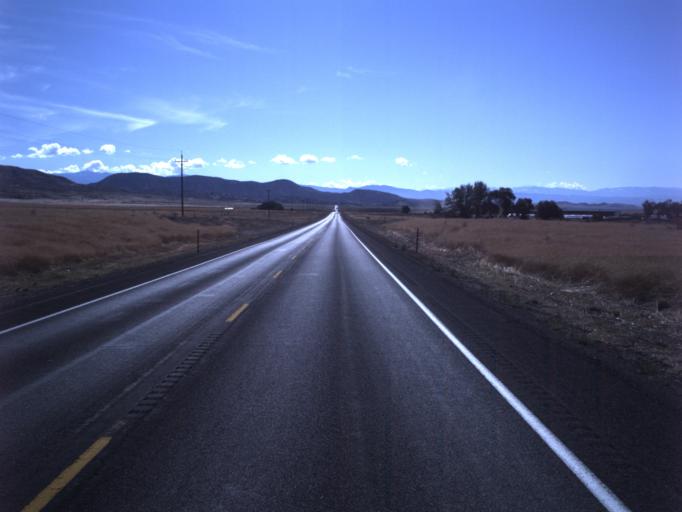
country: US
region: Utah
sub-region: Sanpete County
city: Gunnison
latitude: 39.2709
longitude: -111.8724
